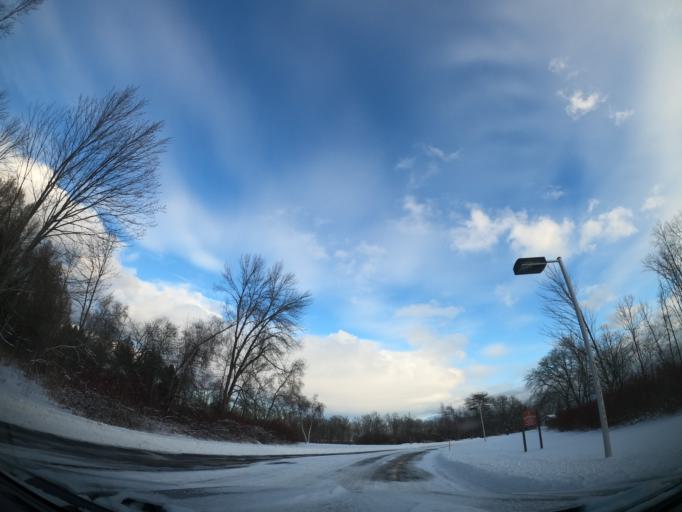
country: US
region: New York
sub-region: Onondaga County
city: Brewerton
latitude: 43.2275
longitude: -76.1116
